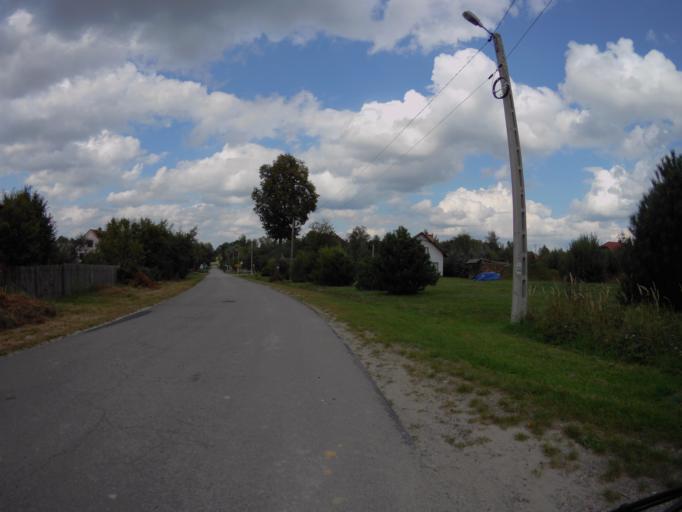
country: PL
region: Subcarpathian Voivodeship
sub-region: Powiat lezajski
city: Brzoza Krolewska
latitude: 50.2419
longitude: 22.3281
